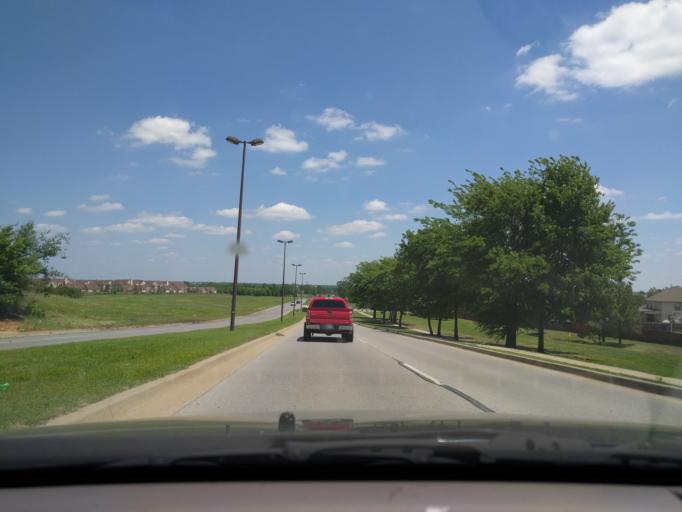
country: US
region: Oklahoma
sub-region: Tulsa County
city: Broken Arrow
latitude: 36.0737
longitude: -95.7882
